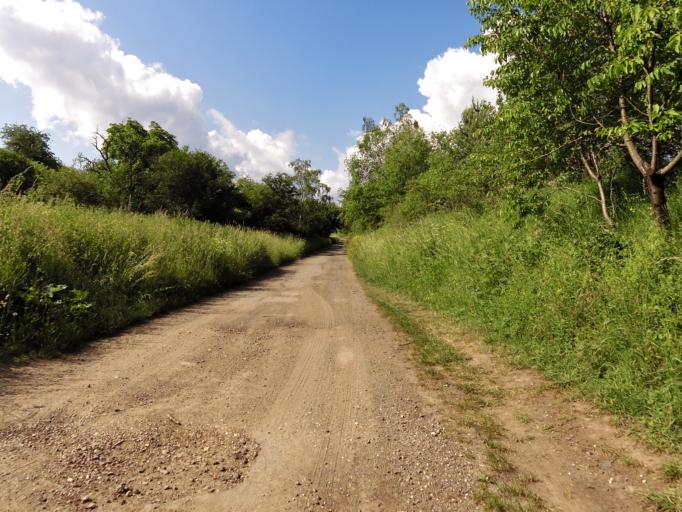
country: DE
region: Rheinland-Pfalz
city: Ebertsheim
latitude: 49.5620
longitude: 8.1115
